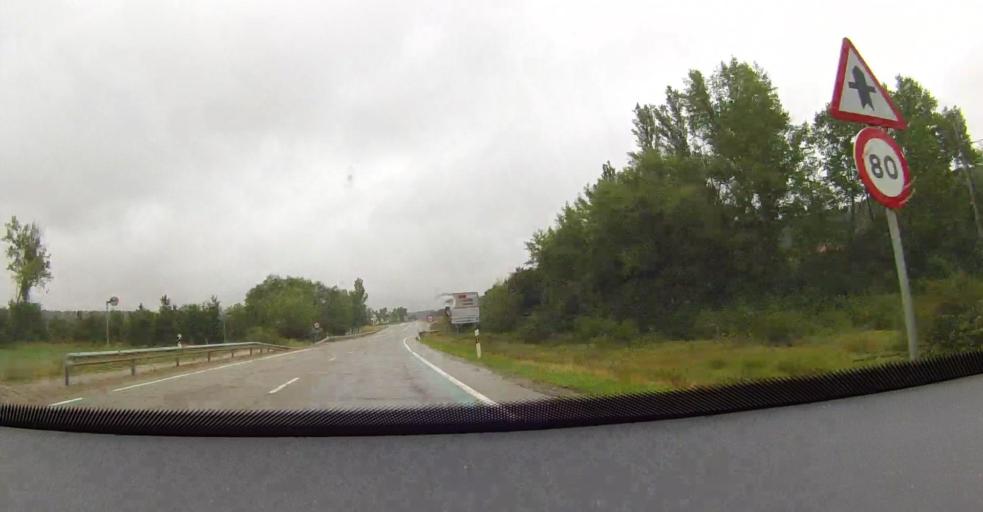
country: ES
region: Castille and Leon
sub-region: Provincia de Palencia
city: Saldana
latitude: 42.5356
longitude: -4.7364
